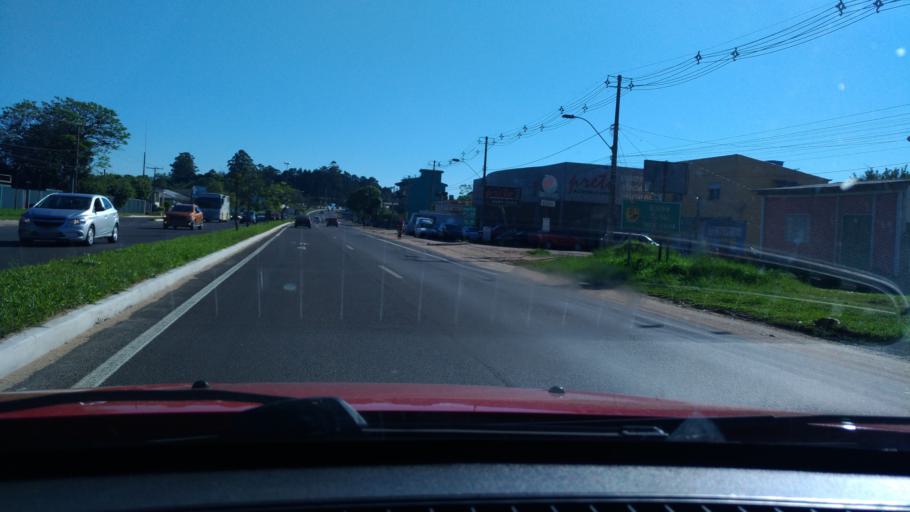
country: BR
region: Rio Grande do Sul
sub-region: Viamao
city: Viamao
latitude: -30.0804
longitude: -51.0517
